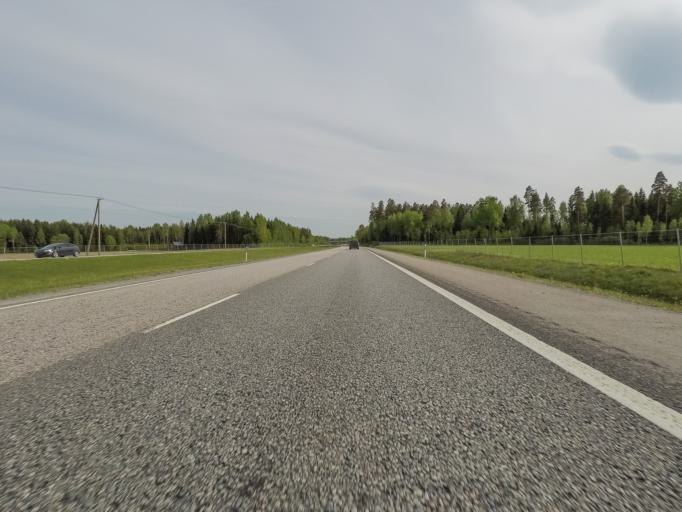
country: FI
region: Uusimaa
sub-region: Helsinki
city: Nurmijaervi
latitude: 60.4784
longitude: 24.8487
